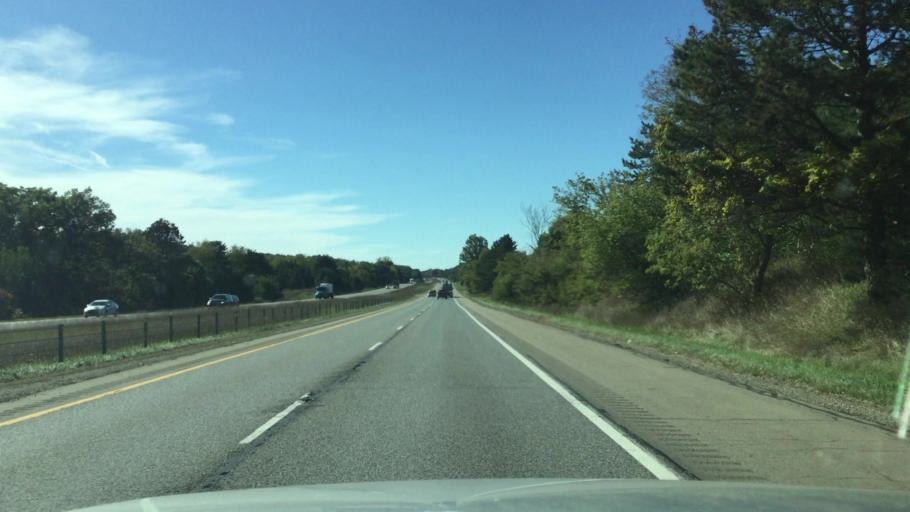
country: US
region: Michigan
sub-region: Washtenaw County
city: Chelsea
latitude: 42.2980
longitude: -84.1023
